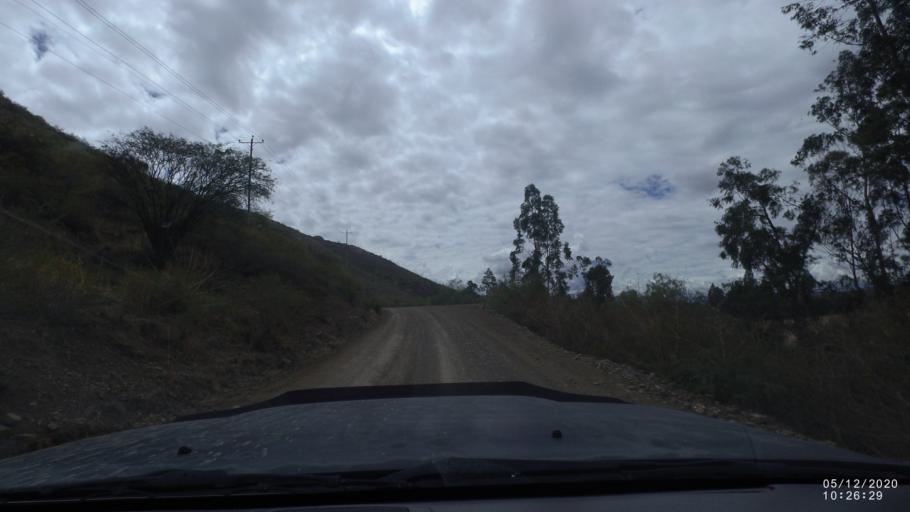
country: BO
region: Cochabamba
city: Sipe Sipe
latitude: -17.5266
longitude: -66.2831
